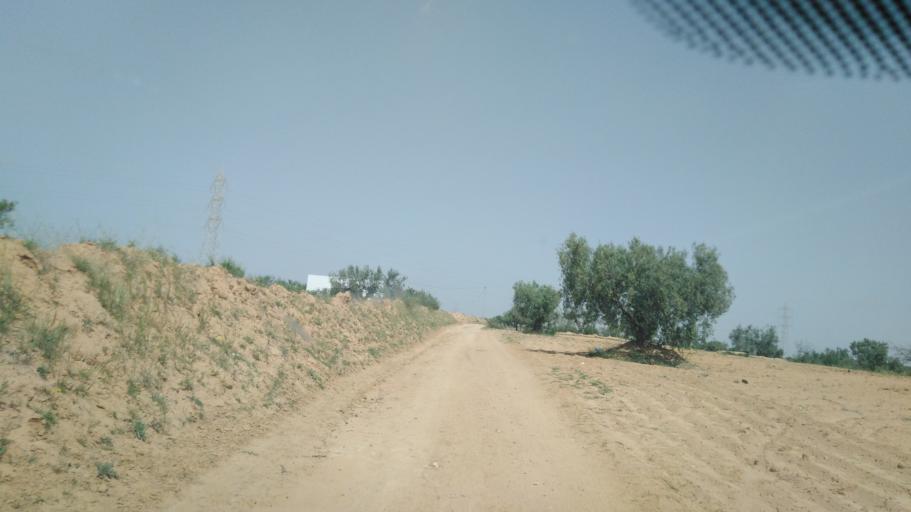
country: TN
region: Safaqis
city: Sfax
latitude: 34.7394
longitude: 10.5721
